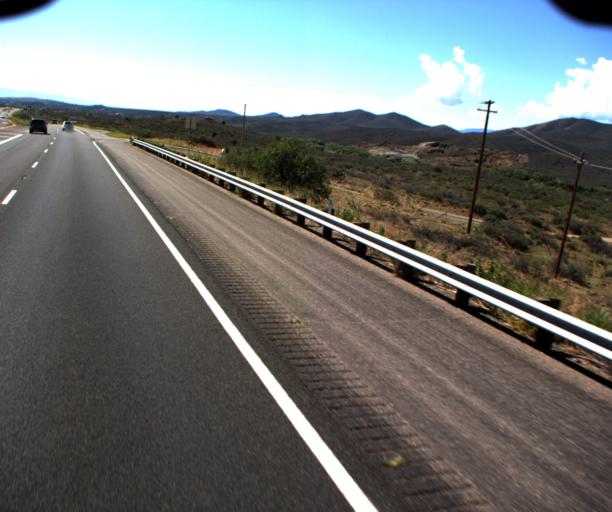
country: US
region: Arizona
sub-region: Yavapai County
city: Mayer
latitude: 34.4366
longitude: -112.2617
